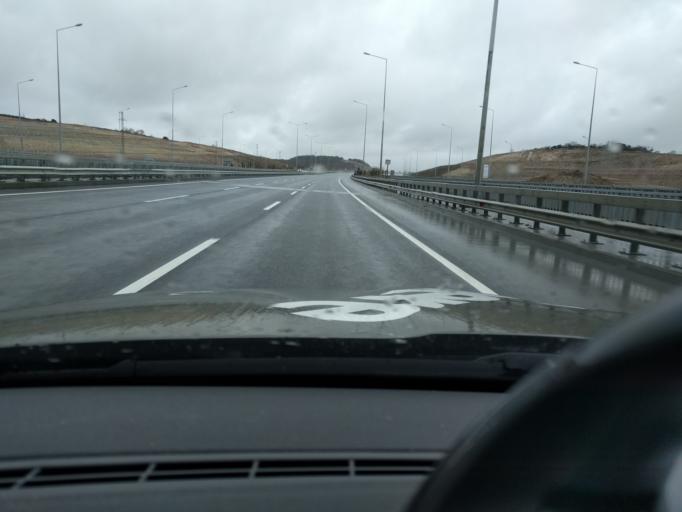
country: TR
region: Istanbul
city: Durusu
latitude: 41.2450
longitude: 28.7670
